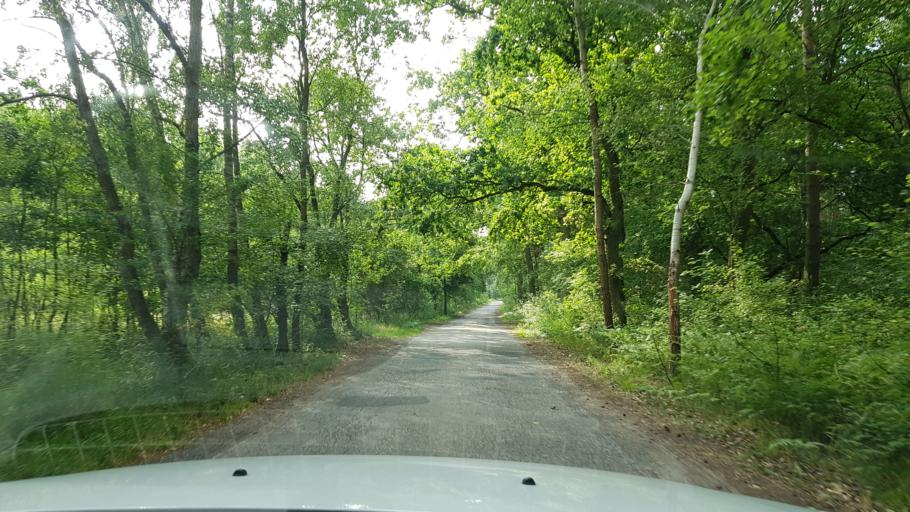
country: PL
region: West Pomeranian Voivodeship
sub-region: Powiat gryfinski
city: Gryfino
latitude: 53.2487
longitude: 14.5594
